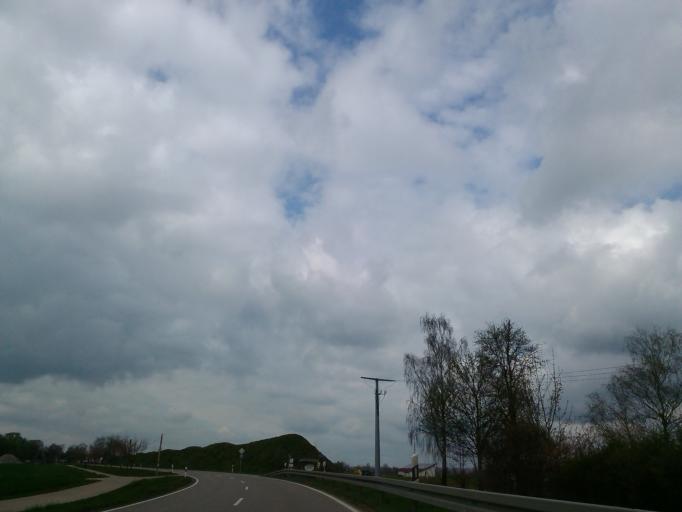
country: DE
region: Bavaria
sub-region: Swabia
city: Leipheim
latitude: 48.4632
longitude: 10.2033
